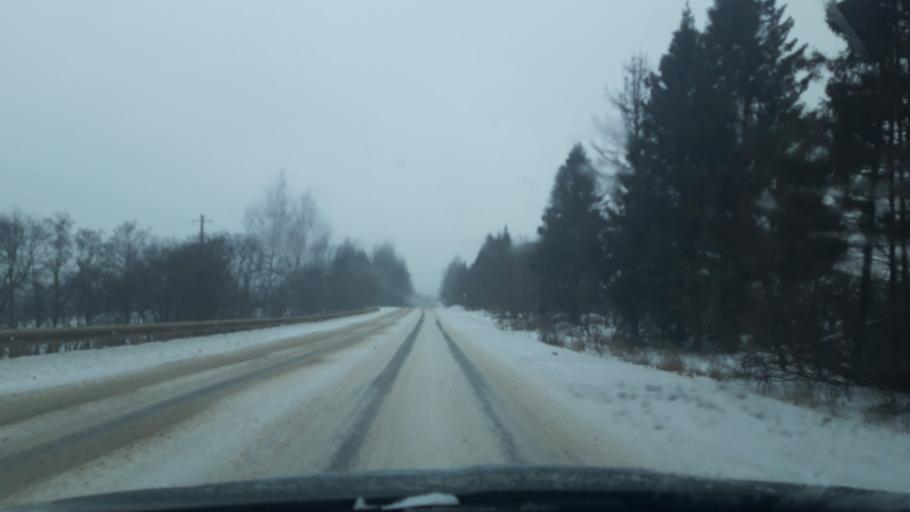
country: RU
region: Moskovskaya
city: Avtopoligon
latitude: 56.2427
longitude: 37.2429
